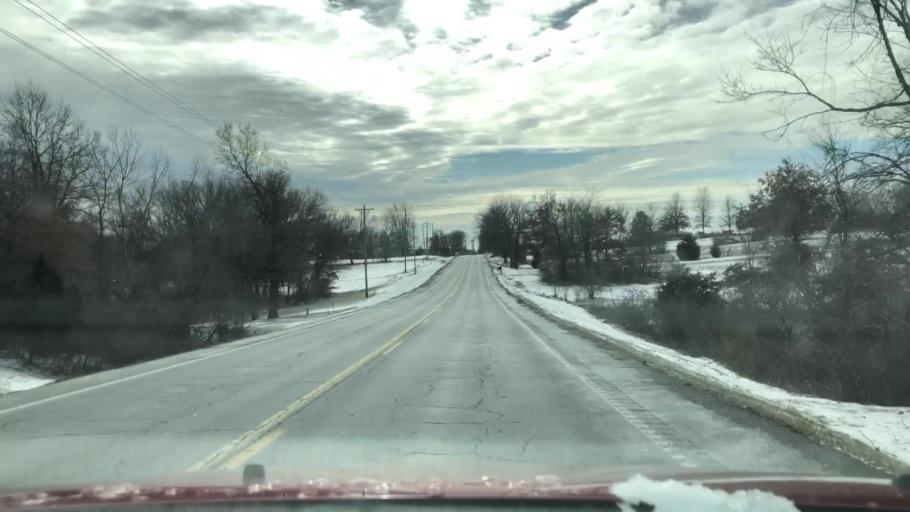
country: US
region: Missouri
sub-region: Jackson County
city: Lone Jack
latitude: 38.8762
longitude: -94.1353
